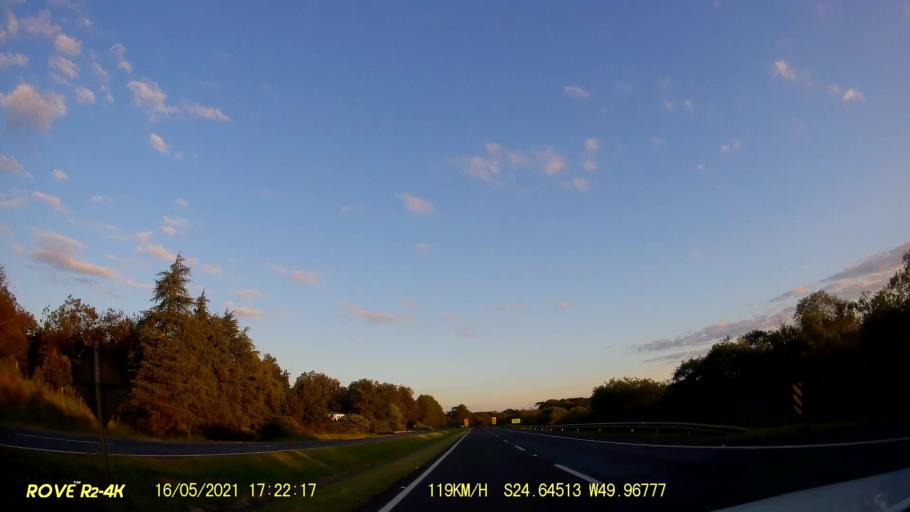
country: BR
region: Parana
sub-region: Pirai Do Sul
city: Pirai do Sul
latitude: -24.6456
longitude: -49.9678
